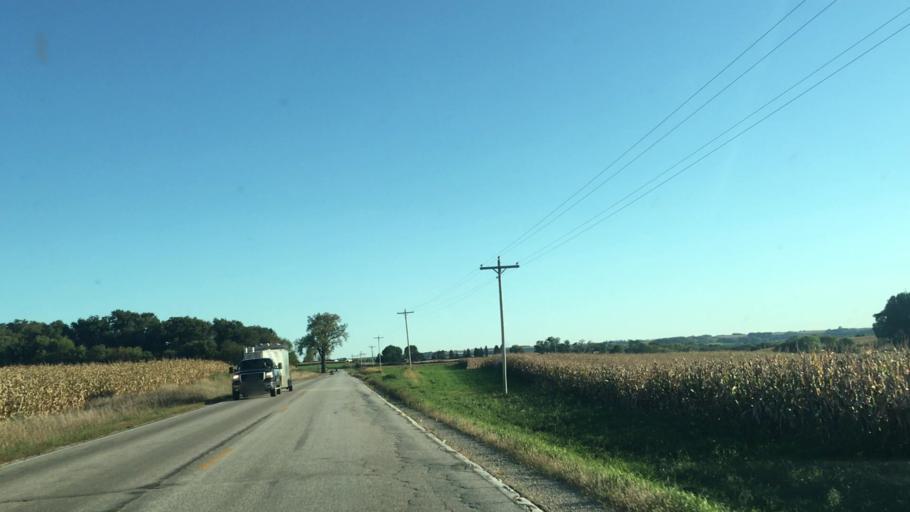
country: US
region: Minnesota
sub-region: Fillmore County
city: Chatfield
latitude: 43.8246
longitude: -92.0694
